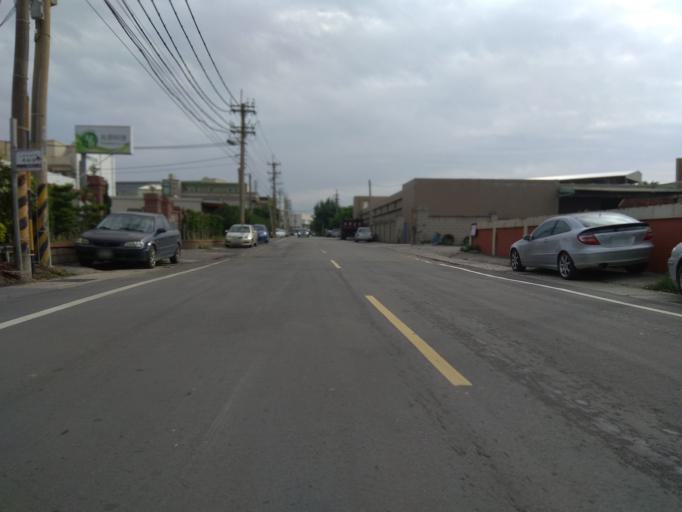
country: TW
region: Taiwan
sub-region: Hsinchu
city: Zhubei
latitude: 24.9860
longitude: 121.0297
